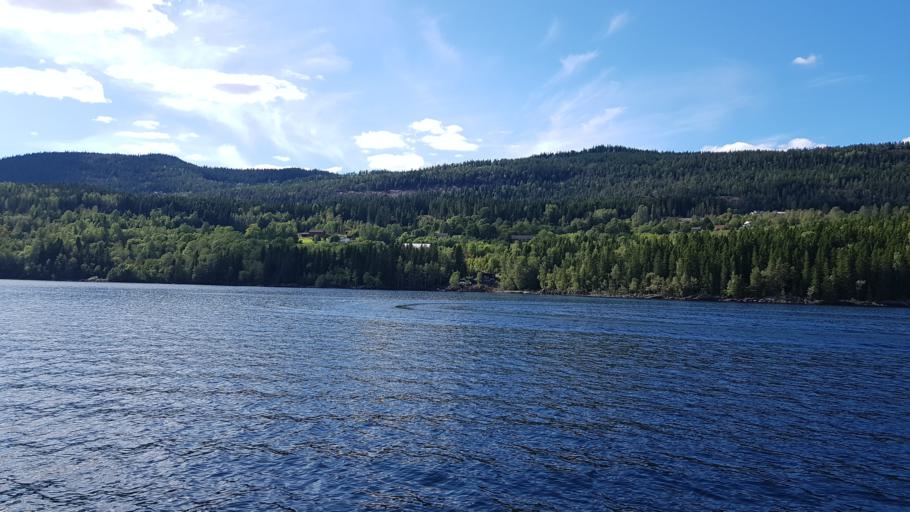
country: NO
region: Akershus
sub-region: Hurdal
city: Hurdal
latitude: 60.5402
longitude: 11.1991
